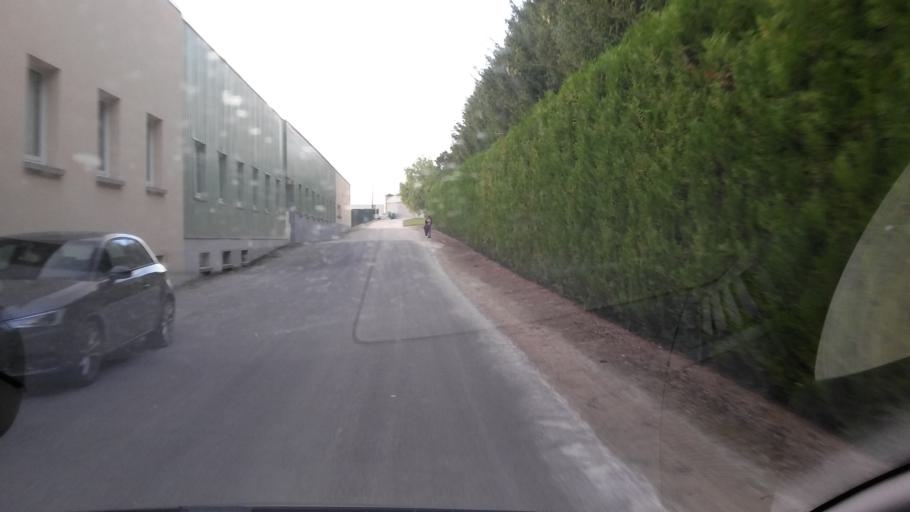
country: FR
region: Champagne-Ardenne
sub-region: Departement de la Marne
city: Fere-Champenoise
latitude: 48.7582
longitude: 3.9927
